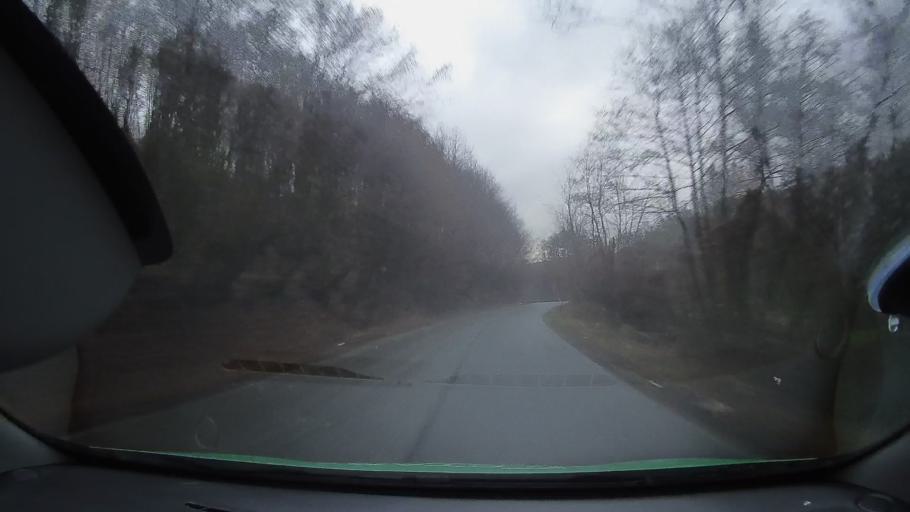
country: RO
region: Hunedoara
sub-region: Comuna Baia de Cris
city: Baia de Cris
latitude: 46.1966
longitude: 22.7172
